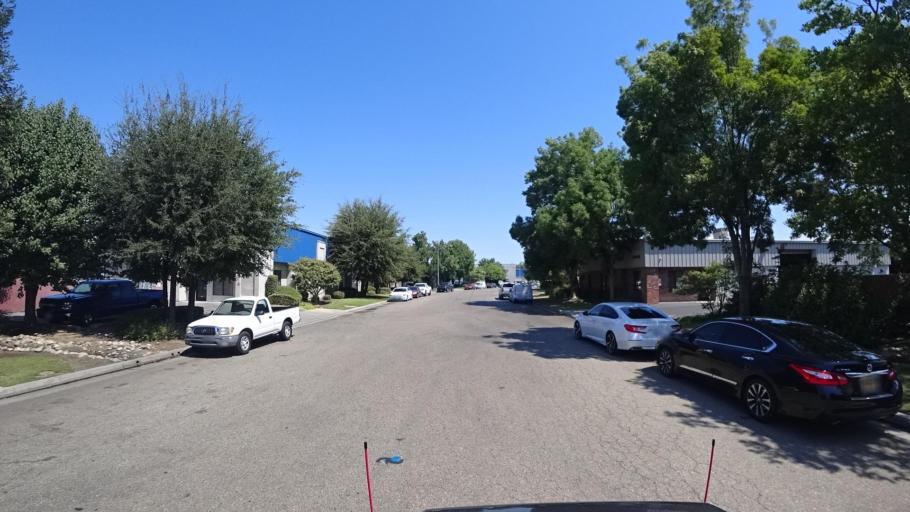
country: US
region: California
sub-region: Fresno County
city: Tarpey Village
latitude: 36.7732
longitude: -119.6857
